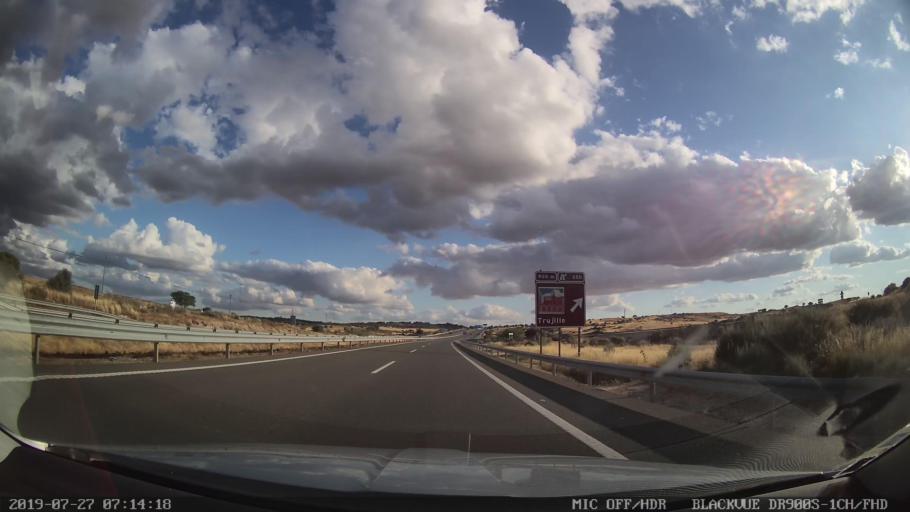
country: ES
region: Extremadura
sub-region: Provincia de Caceres
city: Trujillo
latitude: 39.4956
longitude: -5.8424
